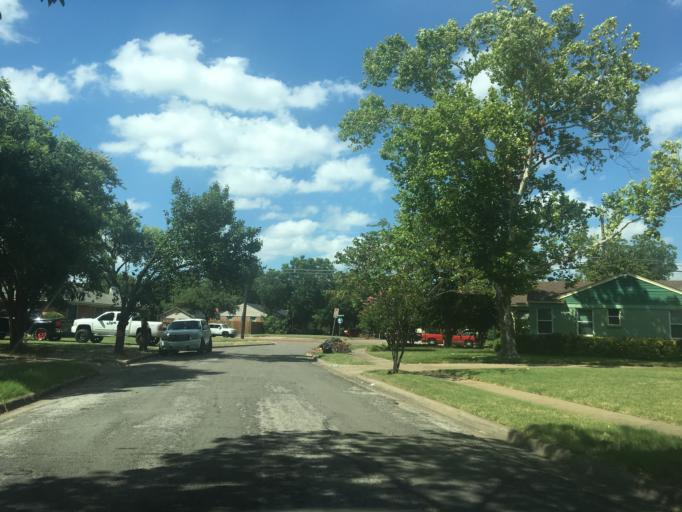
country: US
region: Texas
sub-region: Dallas County
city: Garland
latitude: 32.8357
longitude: -96.6805
